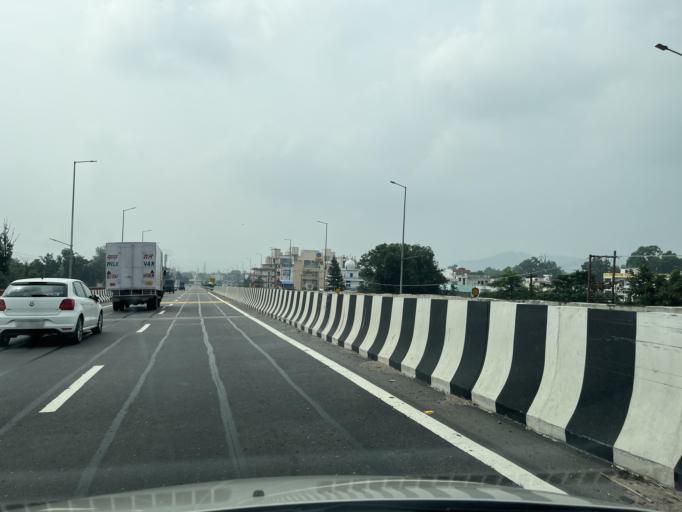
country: IN
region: Uttarakhand
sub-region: Dehradun
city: Raiwala
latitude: 30.0016
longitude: 78.1903
